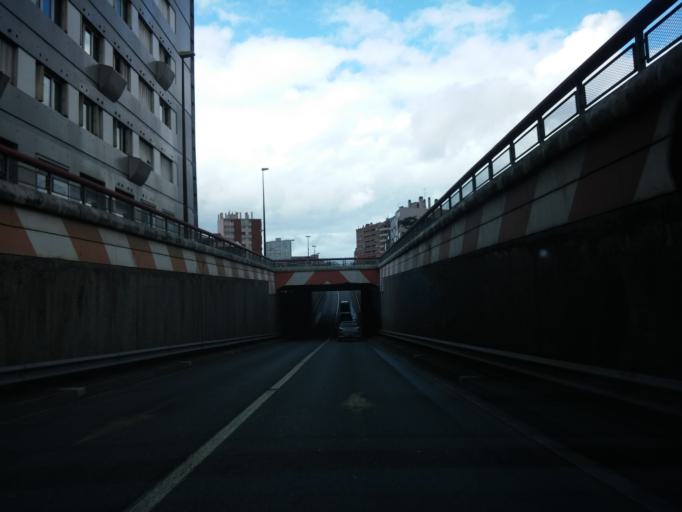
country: FR
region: Midi-Pyrenees
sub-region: Departement de la Haute-Garonne
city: Toulouse
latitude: 43.5933
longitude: 1.4191
